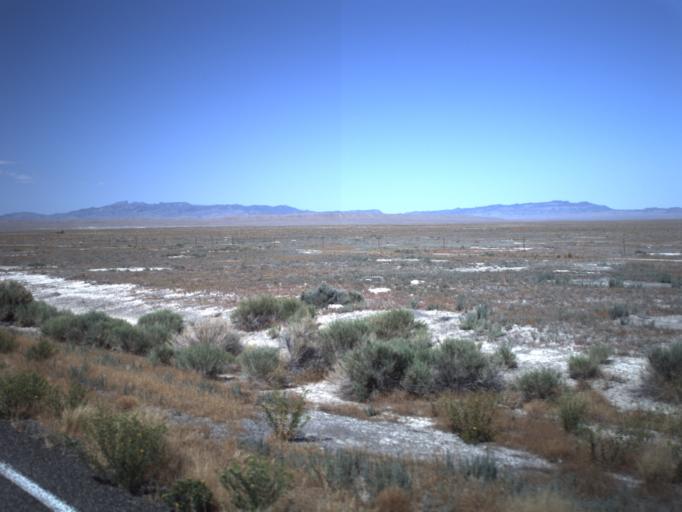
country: US
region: Utah
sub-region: Millard County
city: Delta
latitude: 39.2287
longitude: -112.9348
